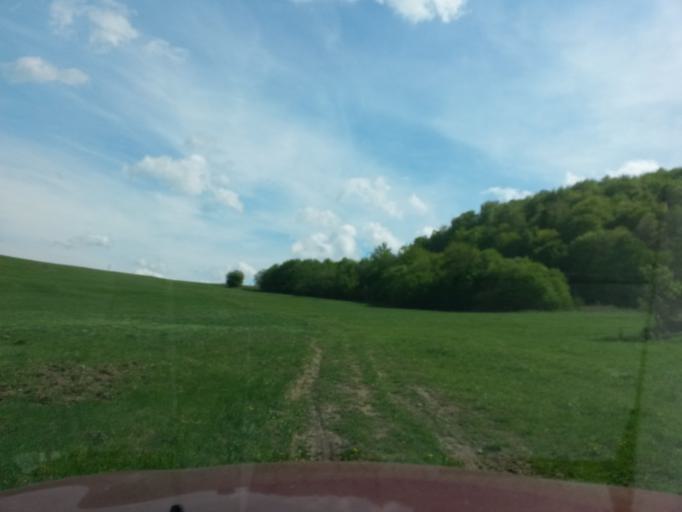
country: SK
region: Kosicky
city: Gelnica
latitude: 48.8313
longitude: 21.0570
